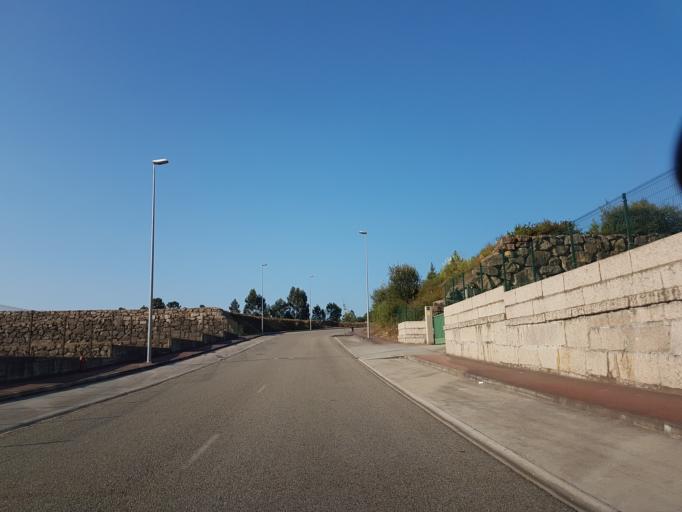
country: ES
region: Galicia
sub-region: Provincia de Pontevedra
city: Porrino
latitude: 42.1866
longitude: -8.6180
